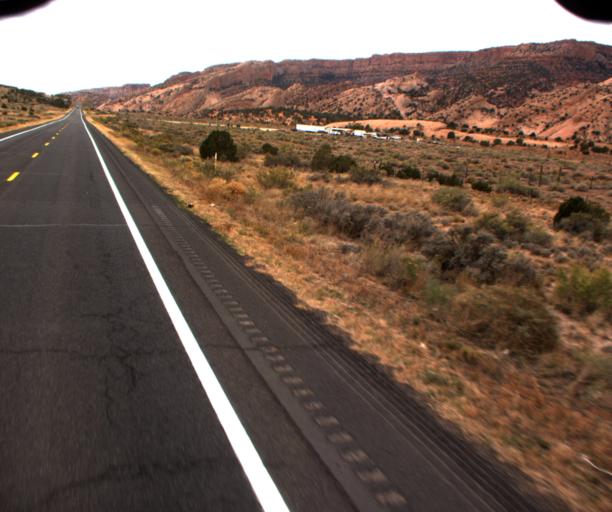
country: US
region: Arizona
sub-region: Navajo County
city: Kayenta
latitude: 36.6714
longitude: -110.4023
